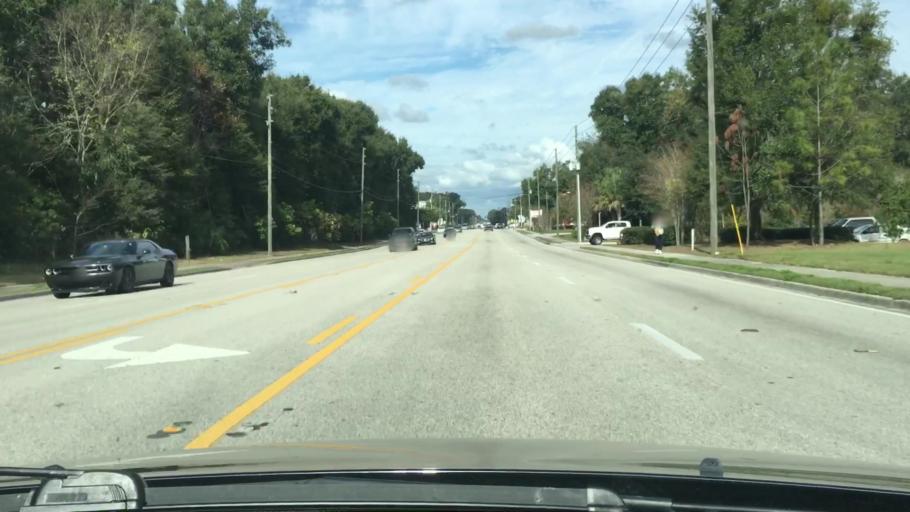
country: US
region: Florida
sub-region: Volusia County
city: DeLand
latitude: 29.0385
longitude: -81.3245
